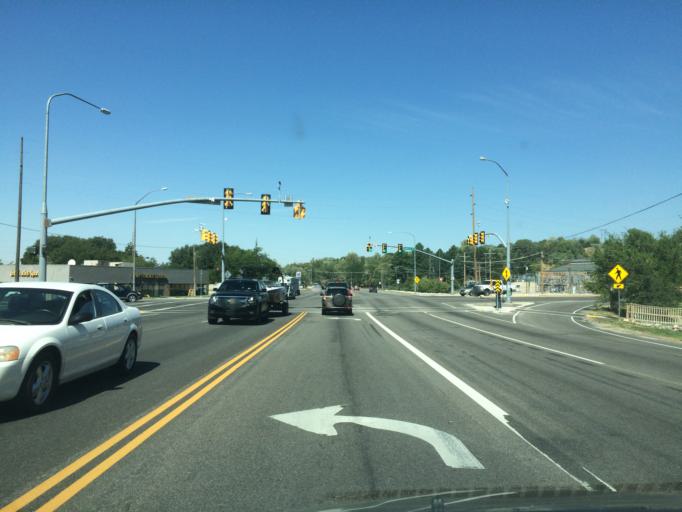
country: US
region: Utah
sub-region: Weber County
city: Ogden
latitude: 41.2416
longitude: -111.9447
